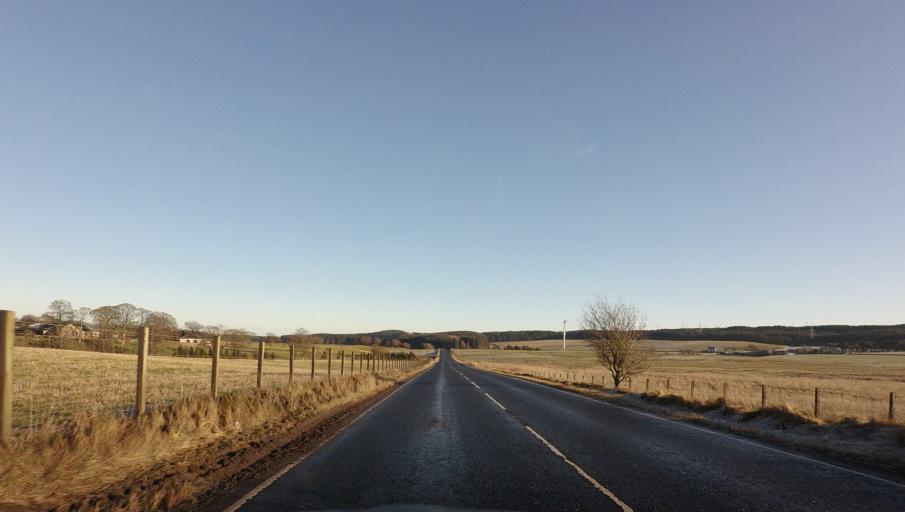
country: GB
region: Scotland
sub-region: West Lothian
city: Fauldhouse
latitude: 55.8095
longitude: -3.7317
